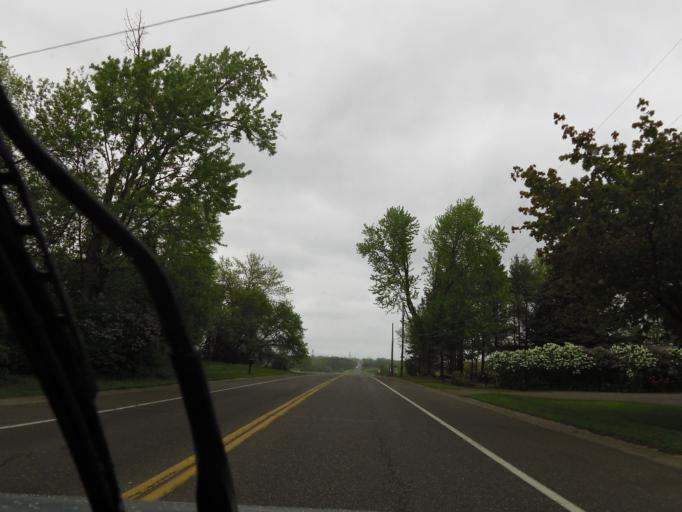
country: US
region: Minnesota
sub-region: Washington County
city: Oak Park Heights
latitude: 45.0207
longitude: -92.8071
